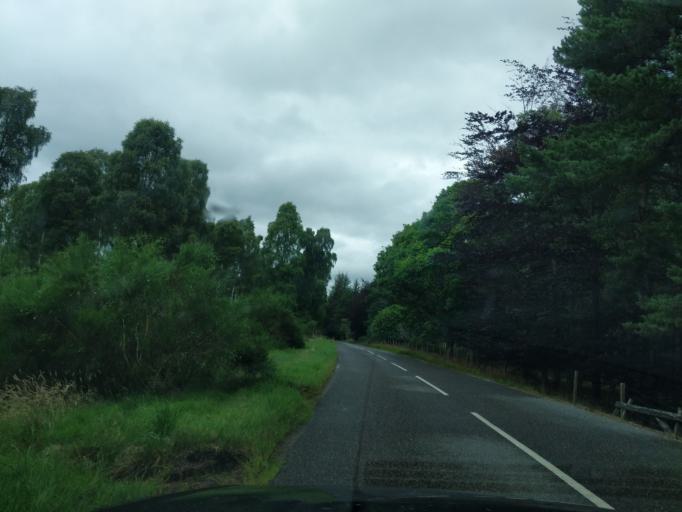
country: GB
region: Scotland
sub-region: Aberdeenshire
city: Aboyne
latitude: 57.0668
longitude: -2.8190
